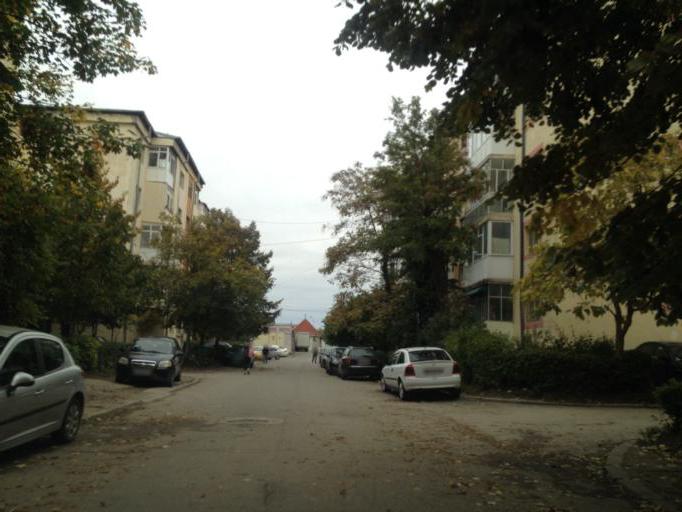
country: RO
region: Dolj
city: Craiova
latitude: 44.3343
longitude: 23.7779
